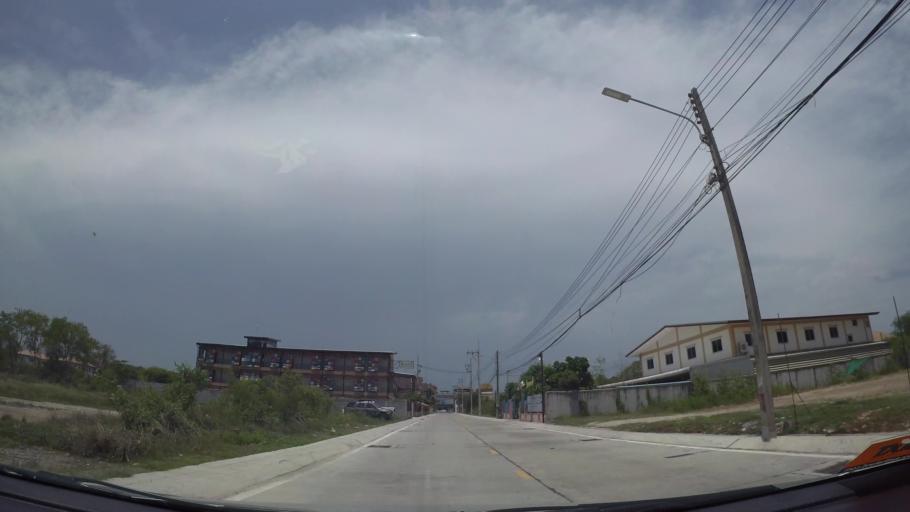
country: TH
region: Chon Buri
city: Chon Buri
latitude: 13.3391
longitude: 100.9470
